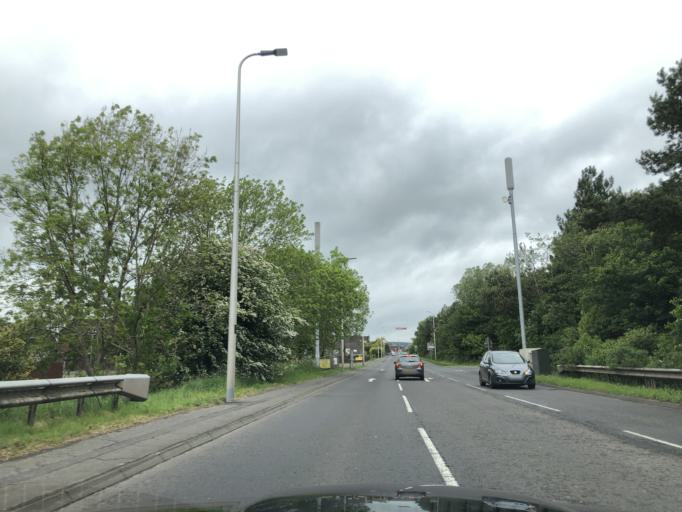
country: GB
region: Northern Ireland
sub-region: Lisburn District
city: Lisburn
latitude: 54.5242
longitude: -6.0742
